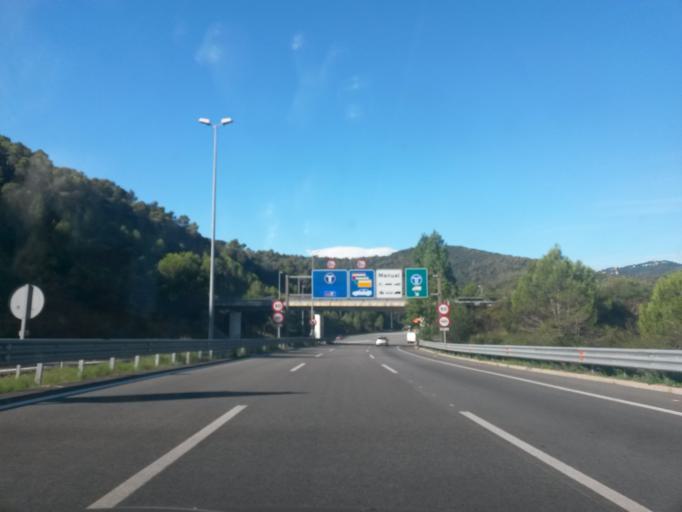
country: ES
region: Catalonia
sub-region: Provincia de Barcelona
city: Santa Susanna
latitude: 41.6536
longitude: 2.7015
